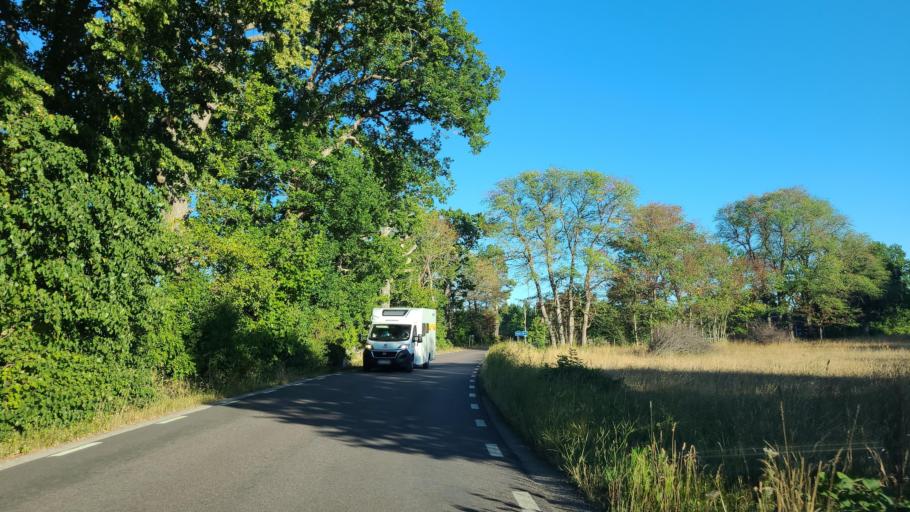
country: SE
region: Kalmar
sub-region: Borgholms Kommun
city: Borgholm
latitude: 57.3149
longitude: 17.0223
